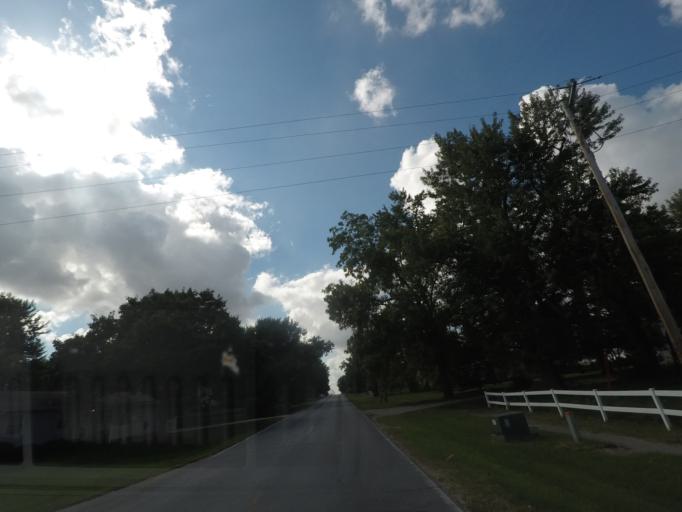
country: US
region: Iowa
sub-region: Story County
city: Nevada
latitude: 42.0153
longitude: -93.3192
